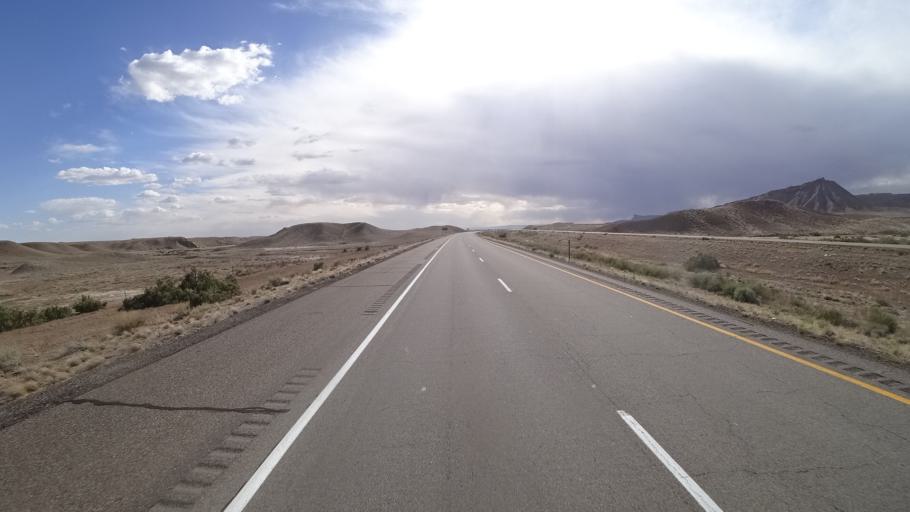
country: US
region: Utah
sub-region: Grand County
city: Moab
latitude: 38.9358
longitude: -109.8407
